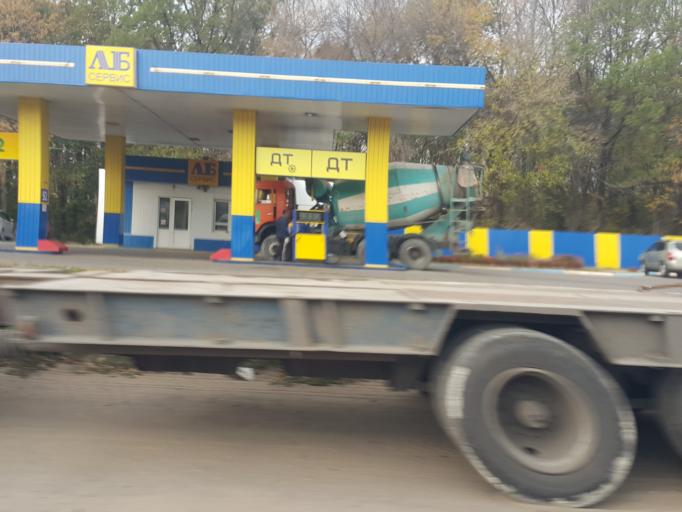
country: RU
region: Tambov
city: Bokino
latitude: 52.6420
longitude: 41.4408
